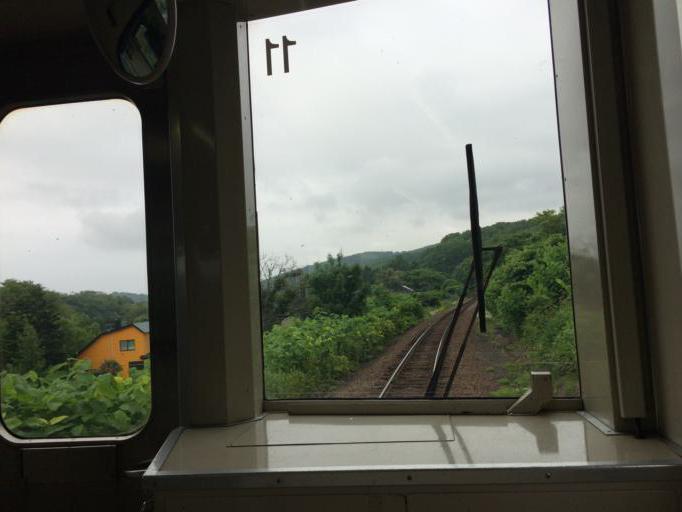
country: JP
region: Hokkaido
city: Otaru
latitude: 43.2126
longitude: 140.9613
